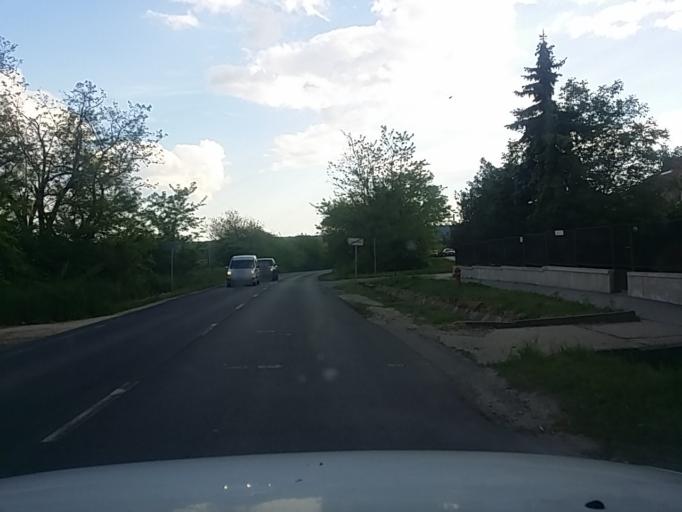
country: HU
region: Pest
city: Mogyorod
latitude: 47.6501
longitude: 19.2361
